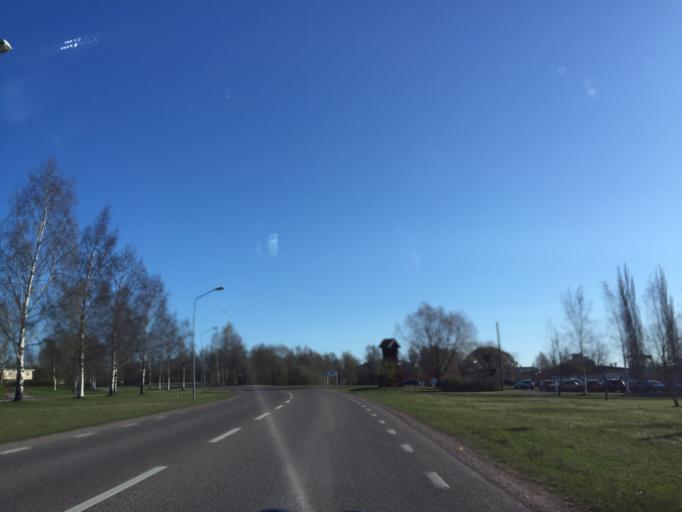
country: SE
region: Dalarna
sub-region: Borlange Kommun
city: Borlaenge
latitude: 60.4786
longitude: 15.4074
